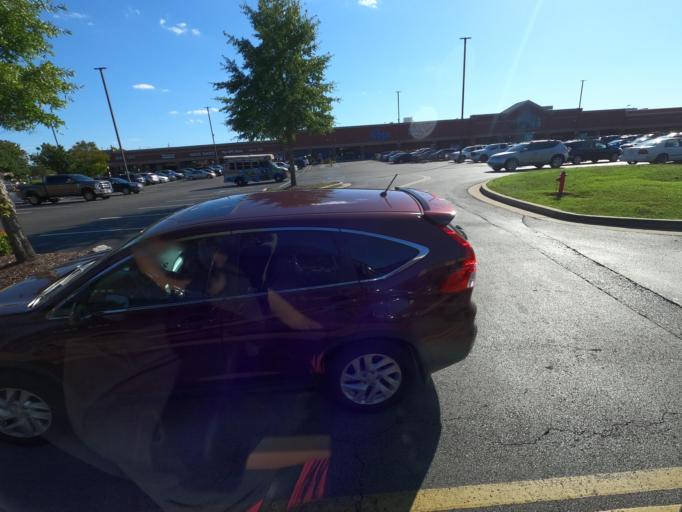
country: US
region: Tennessee
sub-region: Rutherford County
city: Murfreesboro
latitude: 35.8445
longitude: -86.4414
